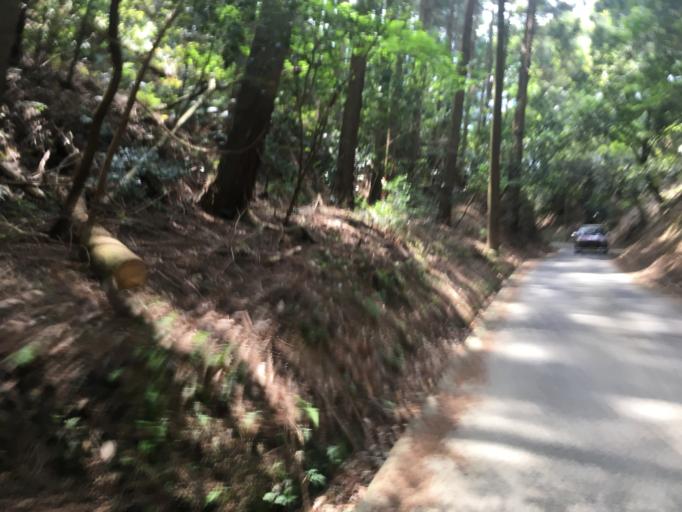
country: JP
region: Kyoto
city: Kameoka
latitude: 35.0296
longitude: 135.6564
